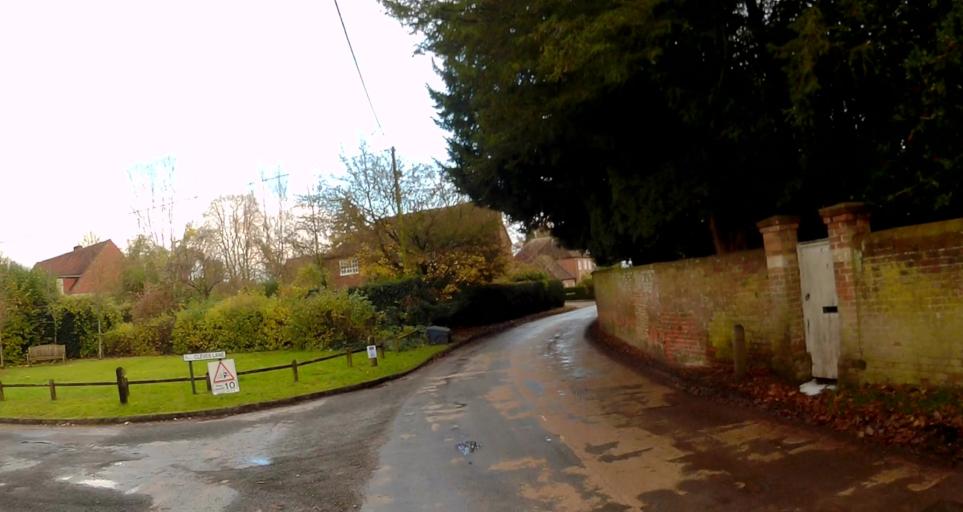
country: GB
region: England
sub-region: Hampshire
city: Old Basing
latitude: 51.2331
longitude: -1.0064
